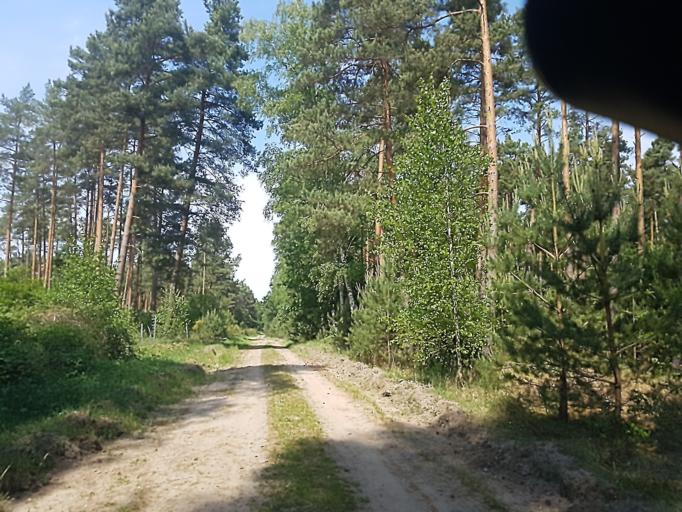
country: DE
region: Brandenburg
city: Gorzke
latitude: 52.0979
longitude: 12.3213
